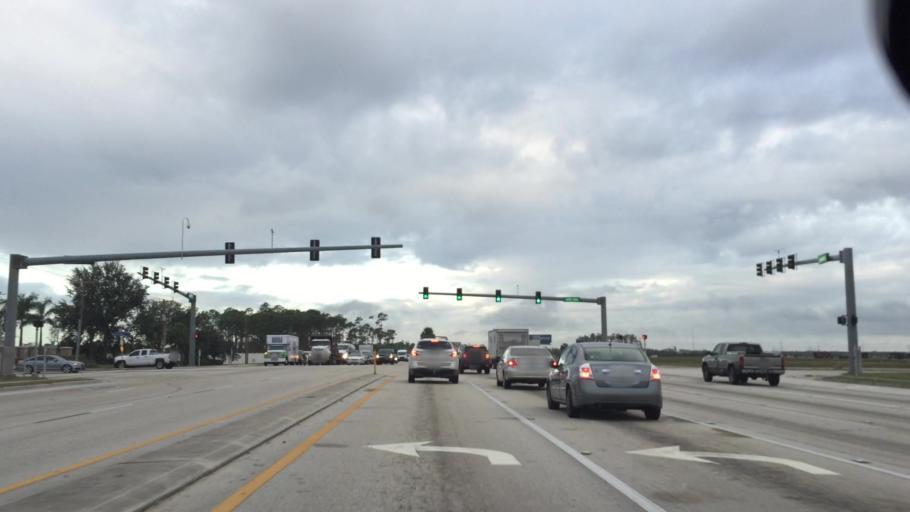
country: US
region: Florida
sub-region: Lee County
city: Three Oaks
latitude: 26.4928
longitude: -81.8002
